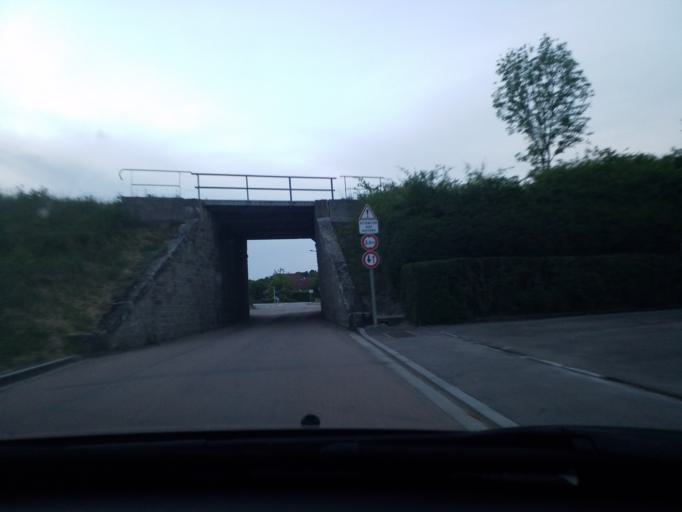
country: FR
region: Lorraine
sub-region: Departement des Vosges
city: Vittel
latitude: 48.2056
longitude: 5.9535
